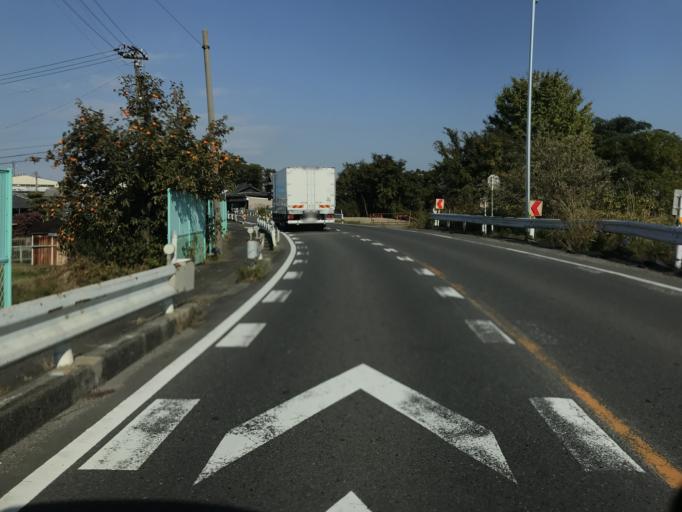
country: JP
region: Aichi
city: Kanie
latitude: 35.1793
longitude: 136.8412
